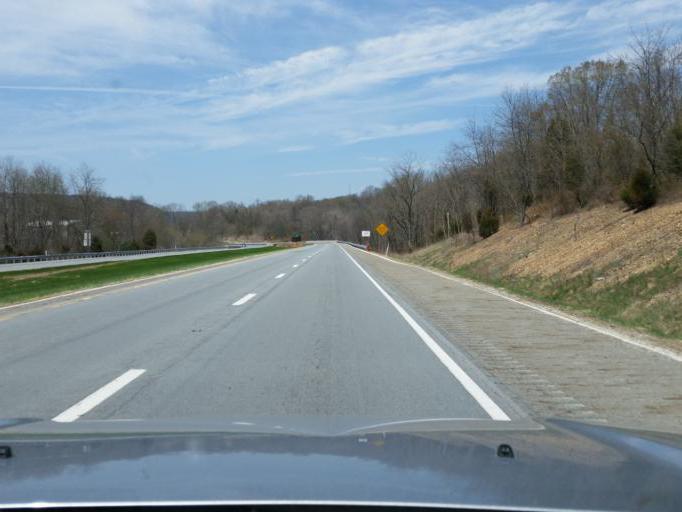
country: US
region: Pennsylvania
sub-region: Perry County
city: Newport
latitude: 40.5382
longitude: -77.1432
